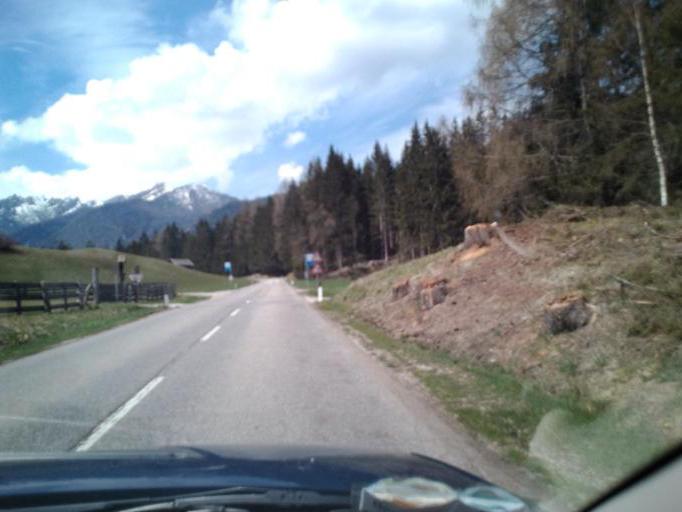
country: IT
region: Trentino-Alto Adige
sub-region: Bolzano
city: Braies
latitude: 46.7166
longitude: 12.1220
